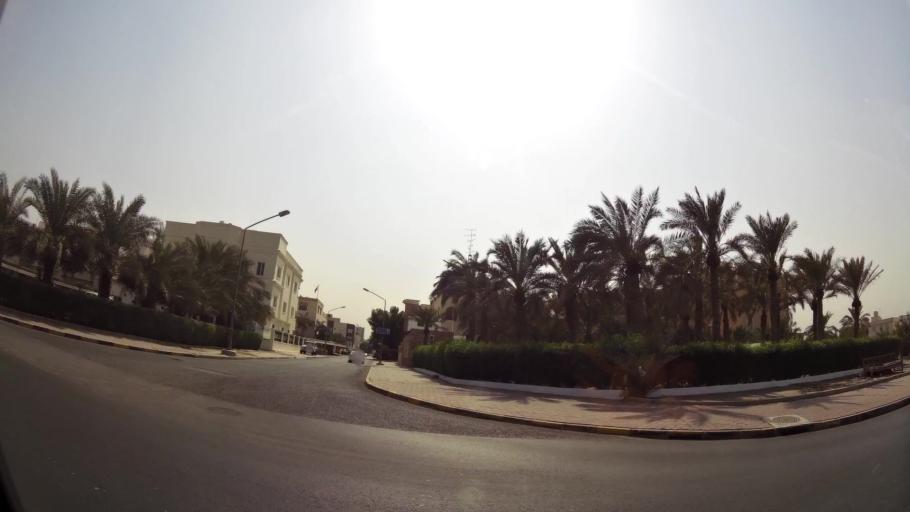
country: KW
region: Al Asimah
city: Ad Dasmah
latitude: 29.3568
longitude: 48.0133
